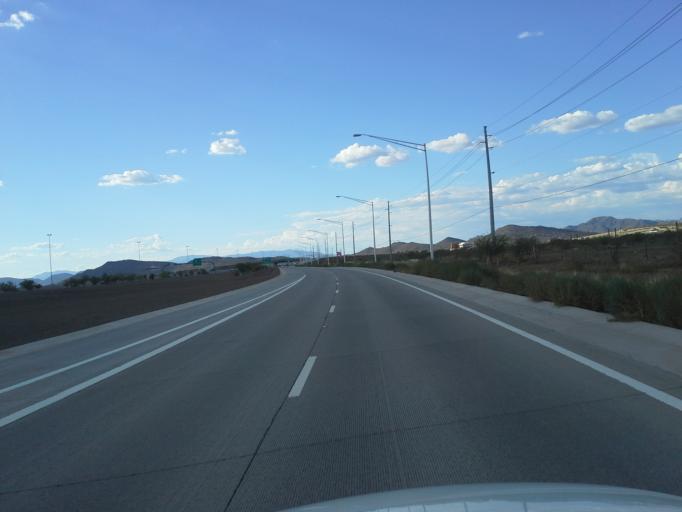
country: US
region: Arizona
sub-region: Maricopa County
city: Anthem
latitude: 33.7737
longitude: -112.1290
